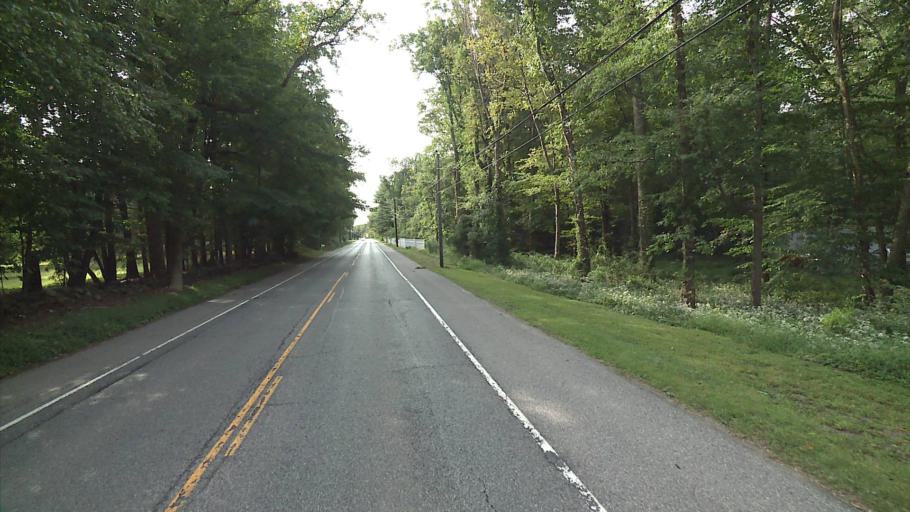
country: US
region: Connecticut
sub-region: Fairfield County
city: New Canaan
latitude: 41.1926
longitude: -73.5068
